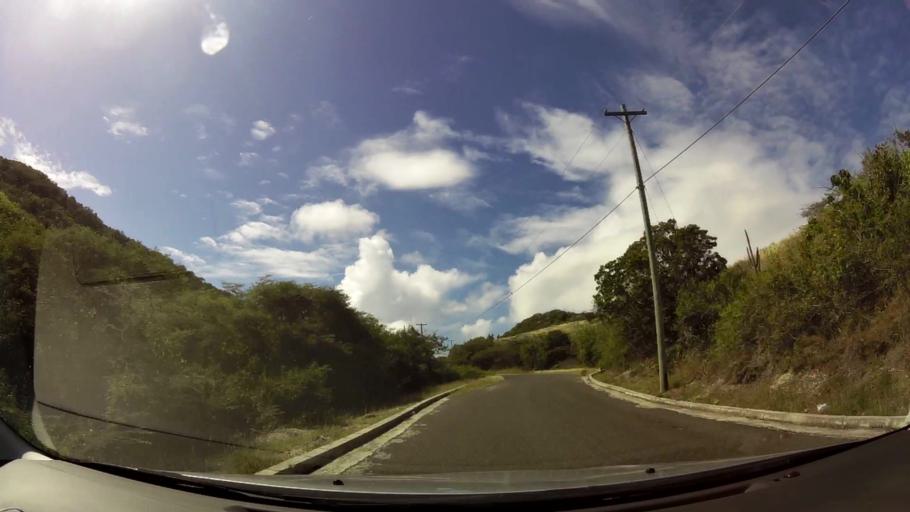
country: AG
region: Saint Paul
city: Falmouth
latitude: 17.0250
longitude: -61.7424
